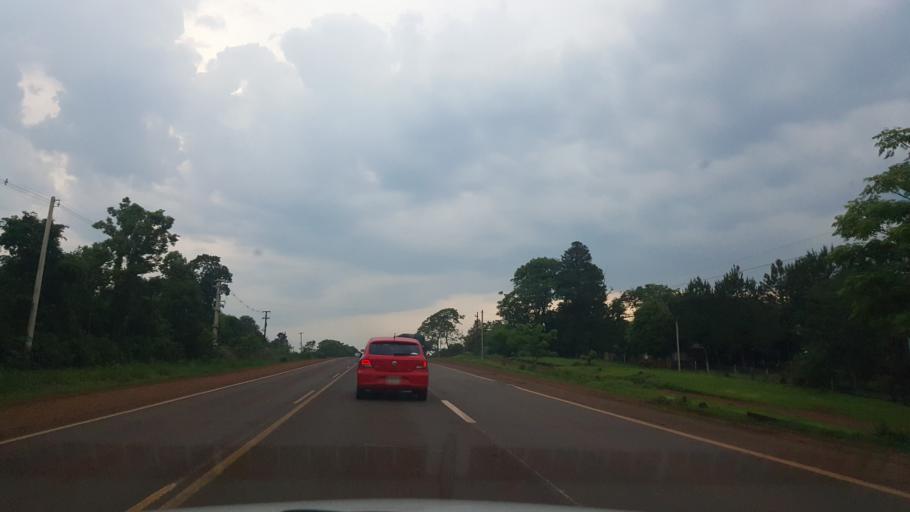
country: AR
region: Misiones
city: Santo Pipo
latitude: -27.1476
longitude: -55.4125
